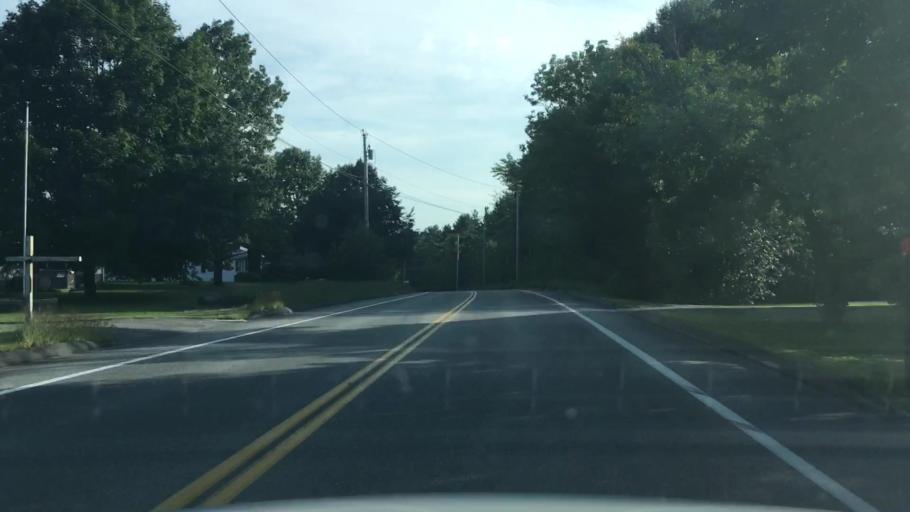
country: US
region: Maine
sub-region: Cumberland County
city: North Windham
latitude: 43.8195
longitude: -70.4407
